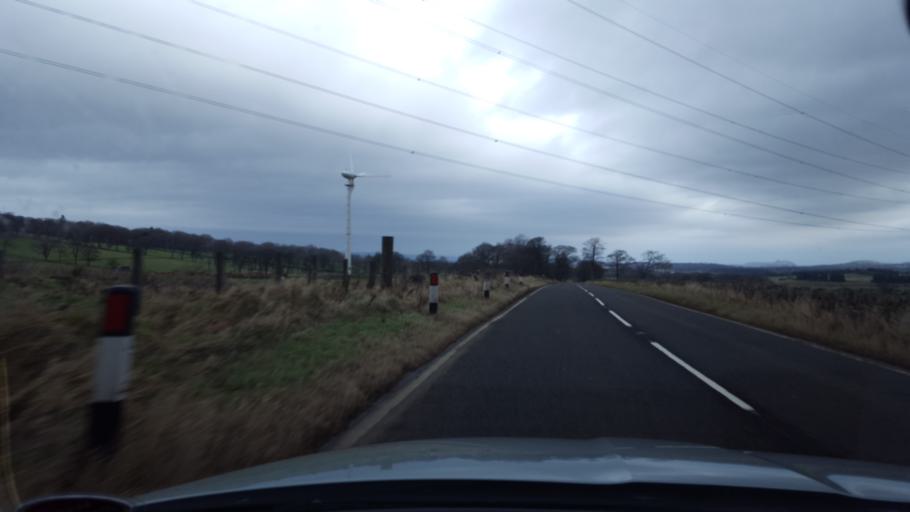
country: GB
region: Scotland
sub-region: West Lothian
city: Kirknewton
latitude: 55.8514
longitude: -3.4358
